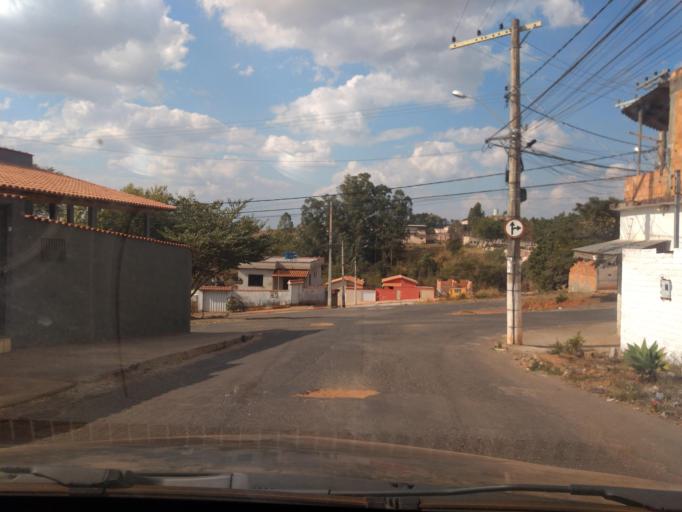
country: BR
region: Minas Gerais
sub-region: Tres Coracoes
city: Tres Coracoes
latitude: -21.6850
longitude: -45.2344
